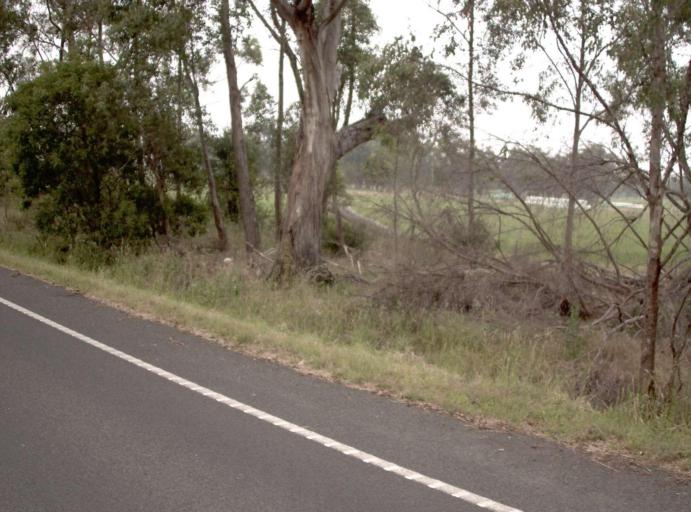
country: AU
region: Victoria
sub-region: Latrobe
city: Morwell
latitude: -38.2808
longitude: 146.3207
